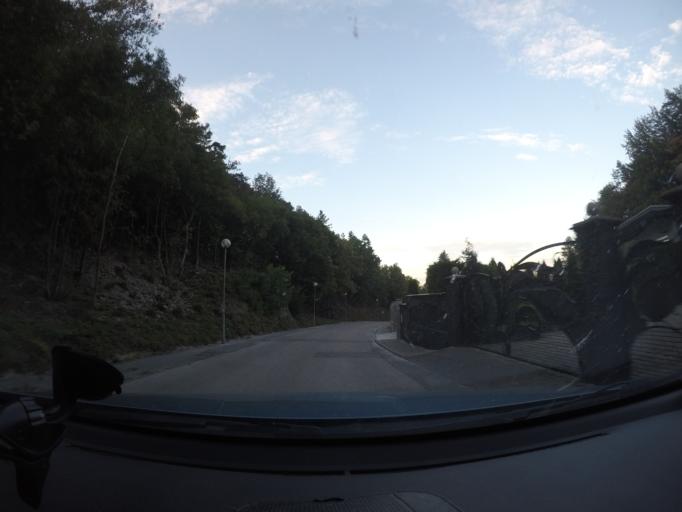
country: SK
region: Trenciansky
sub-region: Okres Trencin
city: Trencin
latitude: 48.8898
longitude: 18.0504
